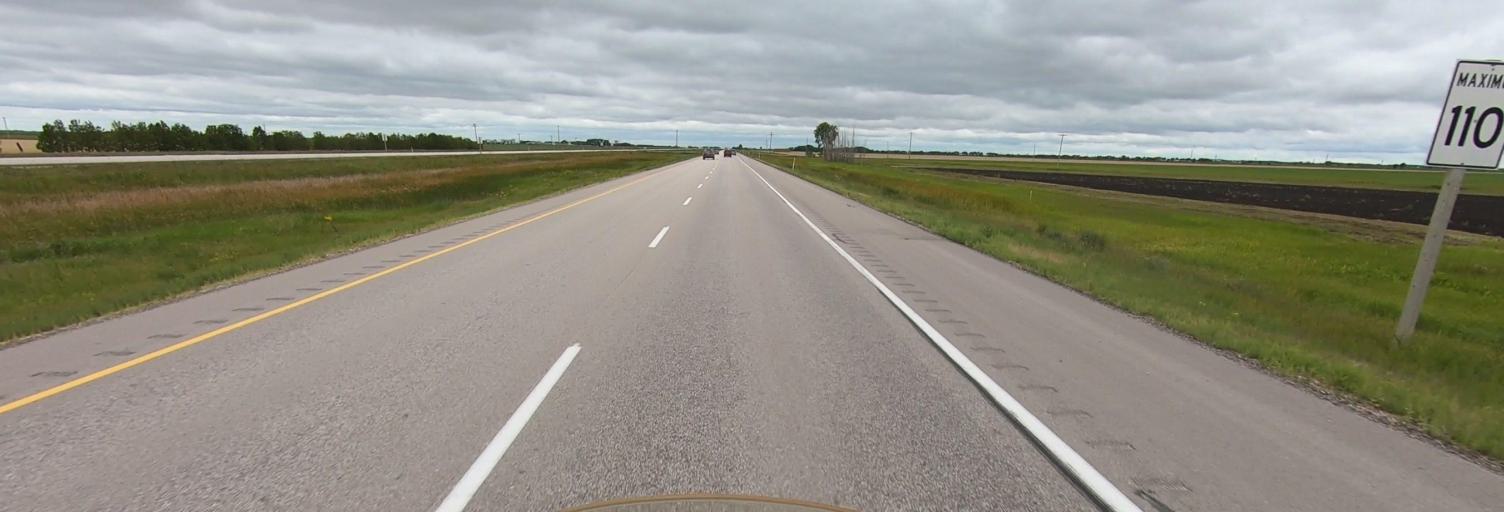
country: CA
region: Manitoba
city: Headingley
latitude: 49.9146
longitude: -97.7979
